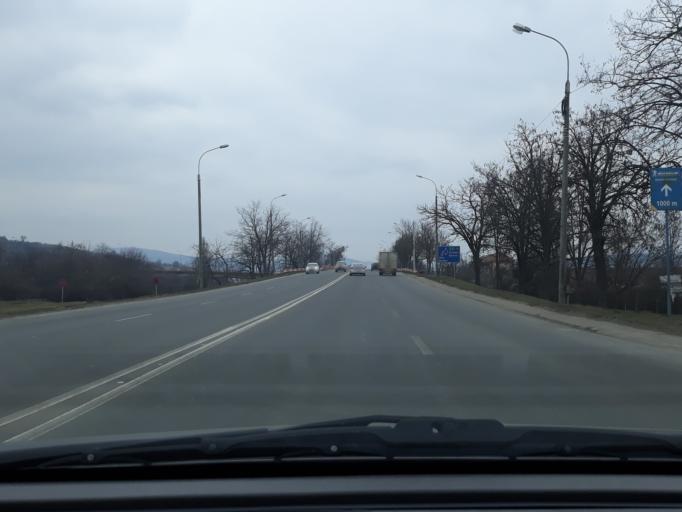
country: RO
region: Salaj
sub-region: Comuna Criseni
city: Criseni
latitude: 47.2199
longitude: 23.0406
